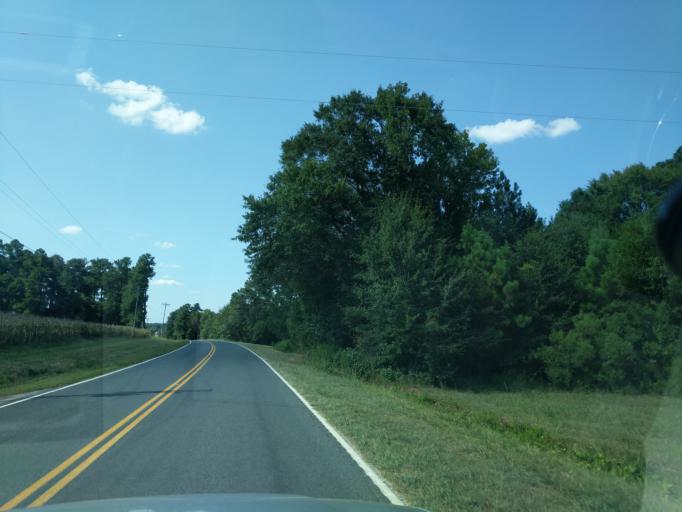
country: US
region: South Carolina
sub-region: Lexington County
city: Leesville
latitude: 34.0190
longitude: -81.5215
